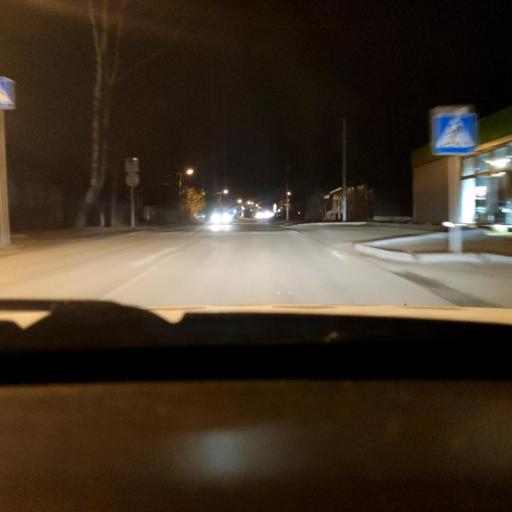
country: RU
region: Perm
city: Perm
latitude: 58.0431
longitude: 56.3273
